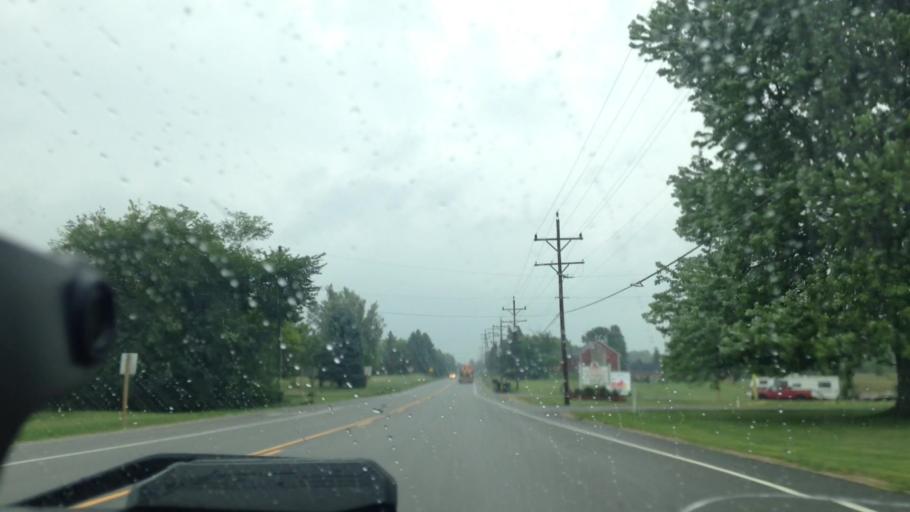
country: US
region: Wisconsin
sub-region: Washington County
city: Slinger
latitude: 43.3216
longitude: -88.2684
